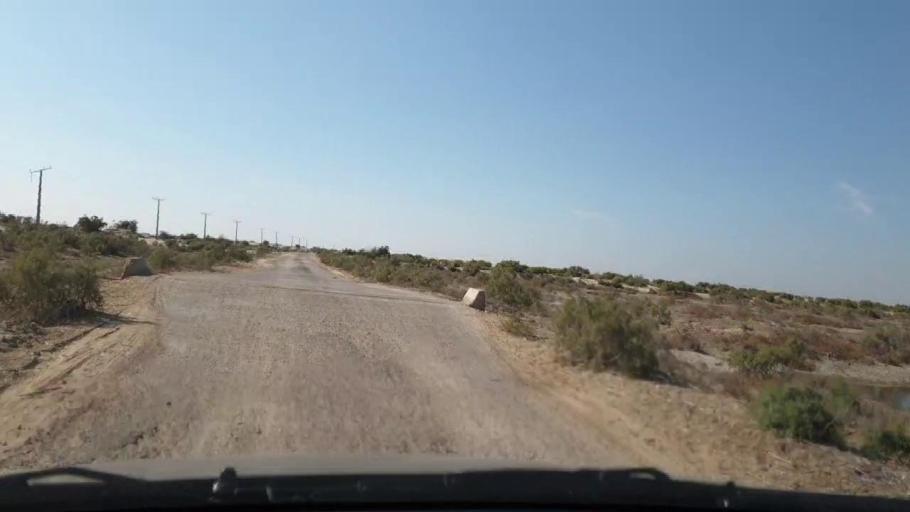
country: PK
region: Sindh
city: Khadro
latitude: 26.2679
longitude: 68.8007
